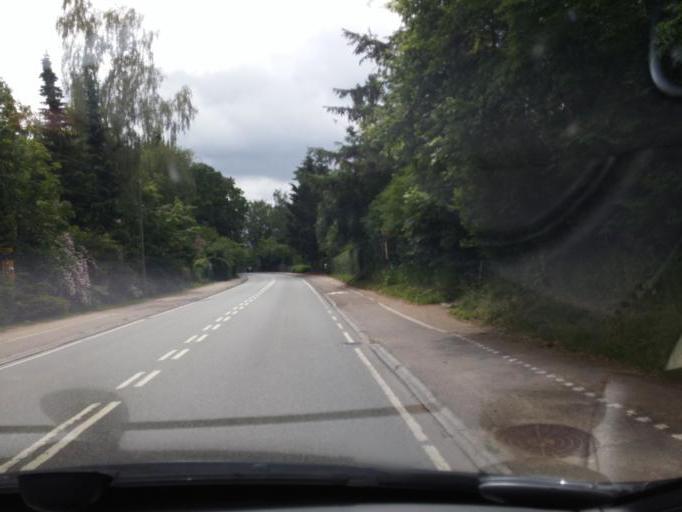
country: DK
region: Capital Region
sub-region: Hillerod Kommune
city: Nodebo
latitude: 55.9741
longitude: 12.3445
